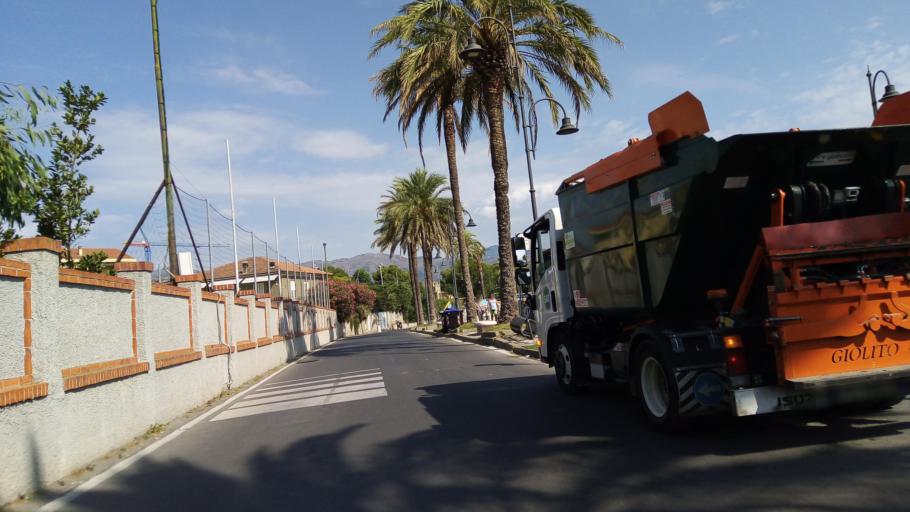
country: IT
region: Liguria
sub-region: Provincia di Savona
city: Albenga
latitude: 44.0493
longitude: 8.2260
